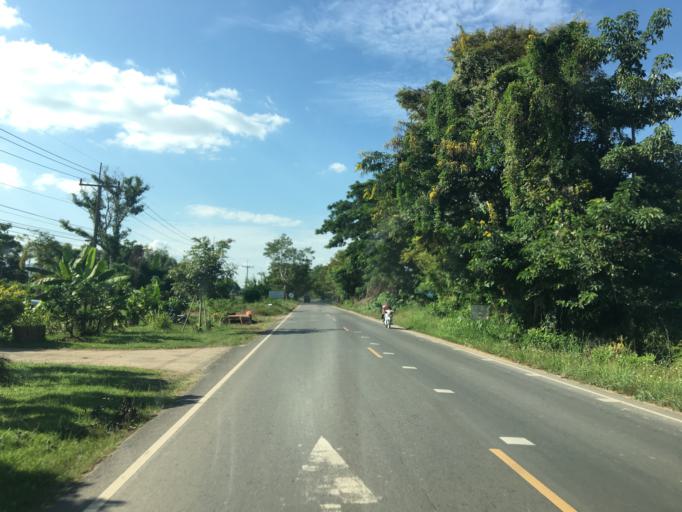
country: TH
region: Phayao
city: Chun
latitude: 19.3278
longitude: 100.1435
